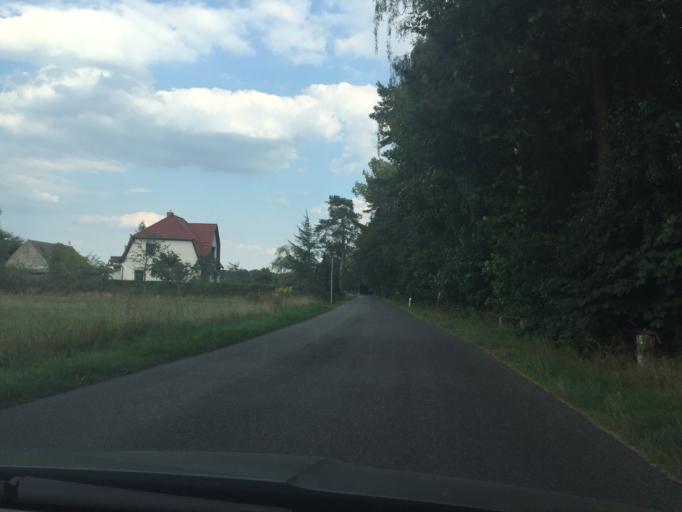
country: DE
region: Brandenburg
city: Spreenhagen
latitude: 52.3441
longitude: 13.8406
